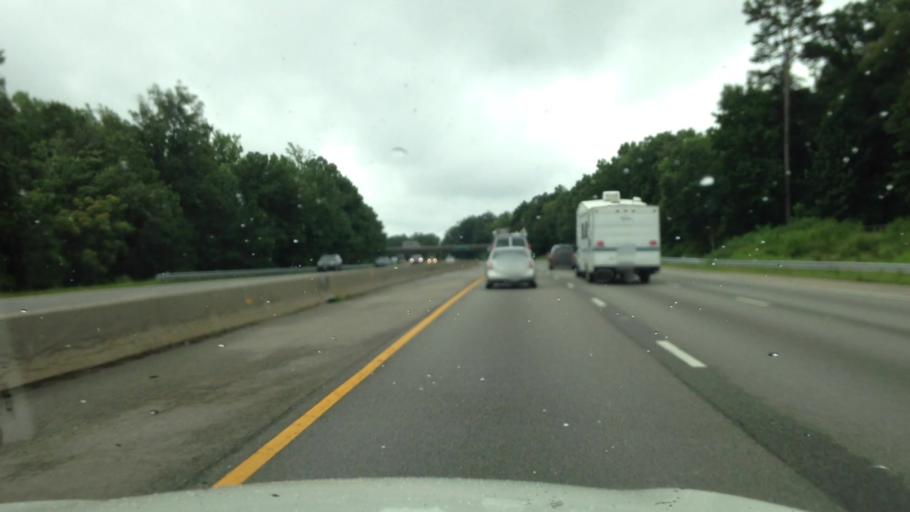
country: US
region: Virginia
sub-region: Chesterfield County
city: Chester
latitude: 37.3464
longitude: -77.4057
